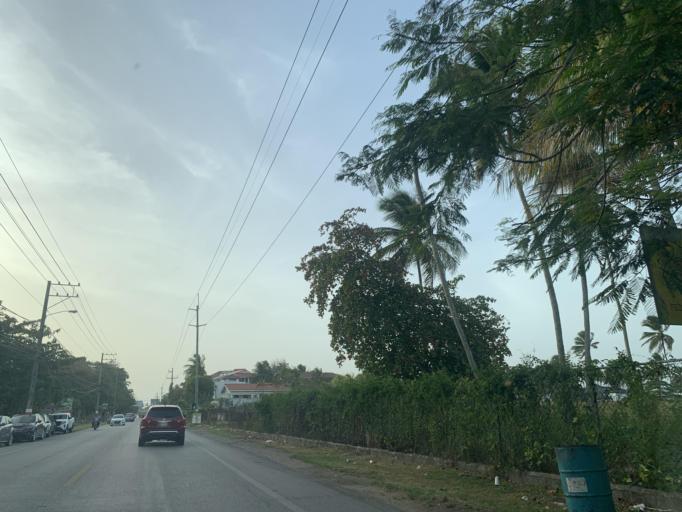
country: DO
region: Puerto Plata
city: Cabarete
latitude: 19.7543
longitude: -70.4172
